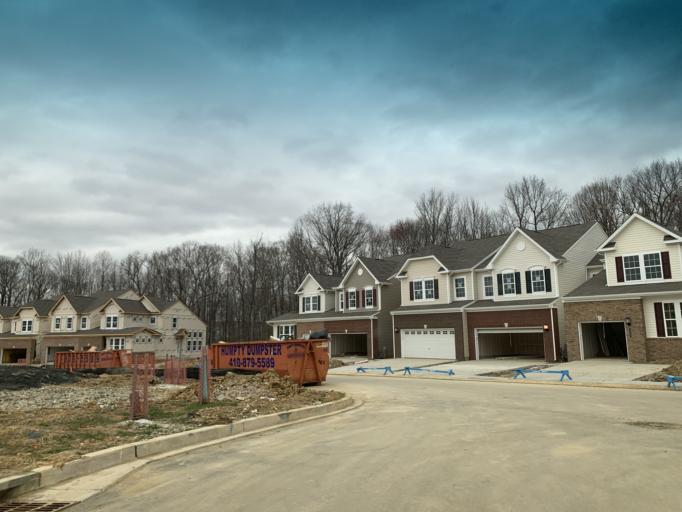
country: US
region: Maryland
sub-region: Harford County
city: Perryman
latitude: 39.4952
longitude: -76.2025
